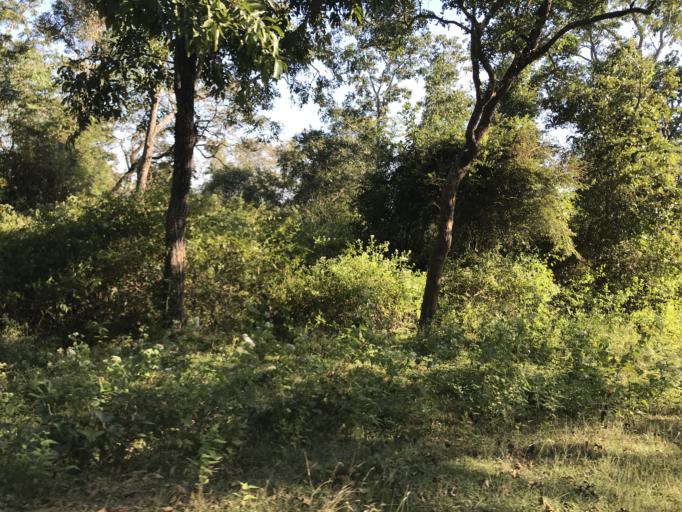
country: IN
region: Karnataka
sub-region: Mysore
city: Heggadadevankote
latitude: 11.9667
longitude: 76.2440
